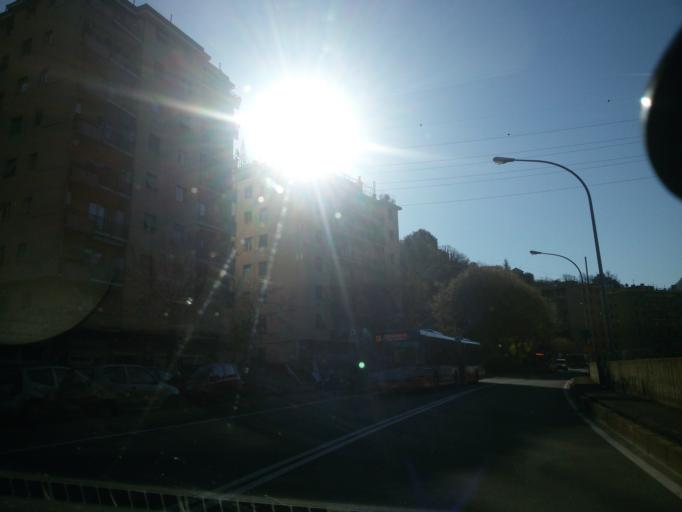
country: IT
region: Liguria
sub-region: Provincia di Genova
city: Piccarello
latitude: 44.4533
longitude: 8.9908
